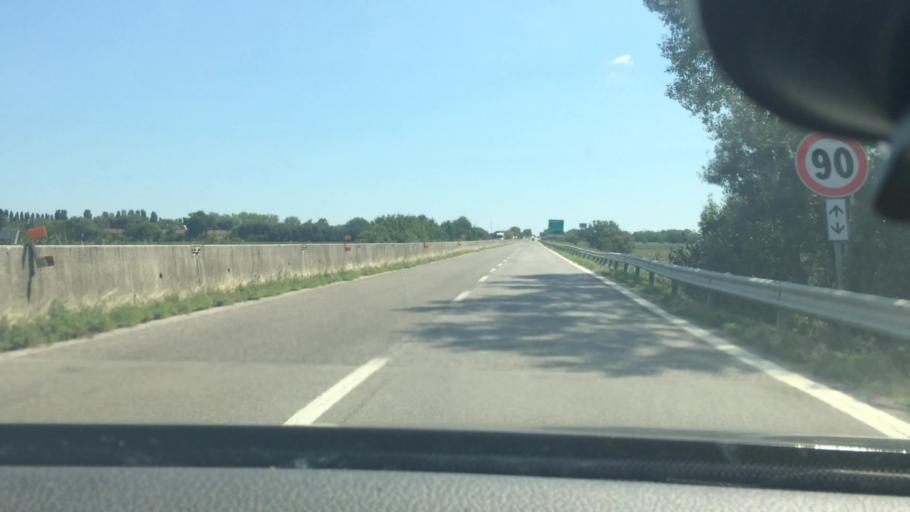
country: IT
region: Emilia-Romagna
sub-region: Provincia di Ferrara
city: Massa Fiscaglia
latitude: 44.7458
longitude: 12.0109
